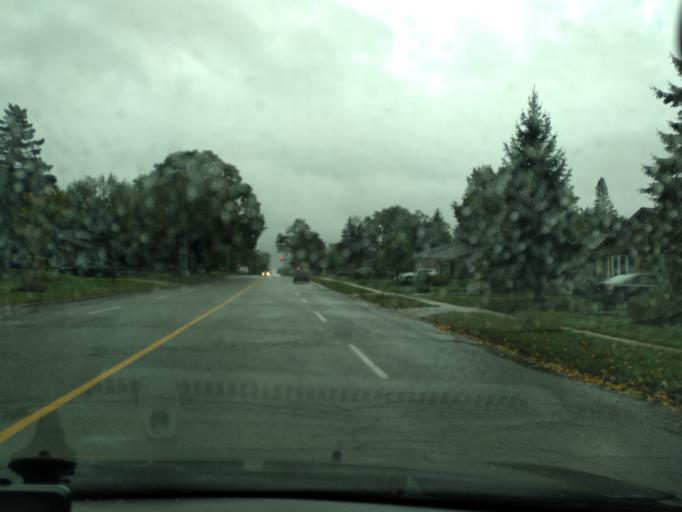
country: CA
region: Ontario
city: Barrie
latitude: 44.4044
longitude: -79.6748
